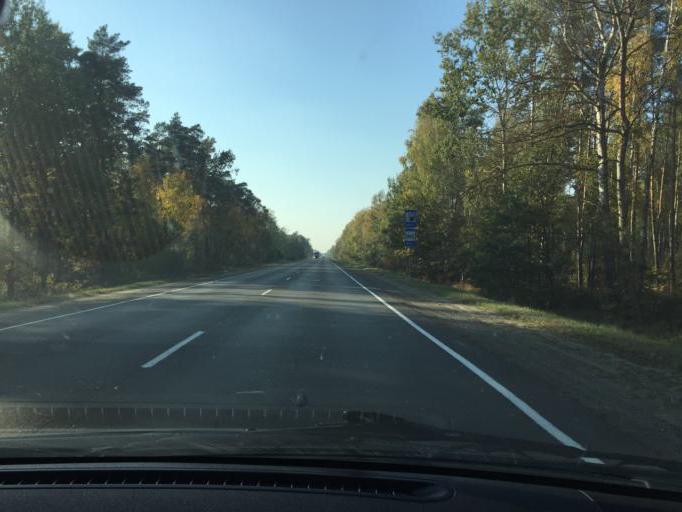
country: BY
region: Brest
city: Mikashevichy
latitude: 52.2424
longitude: 27.4654
